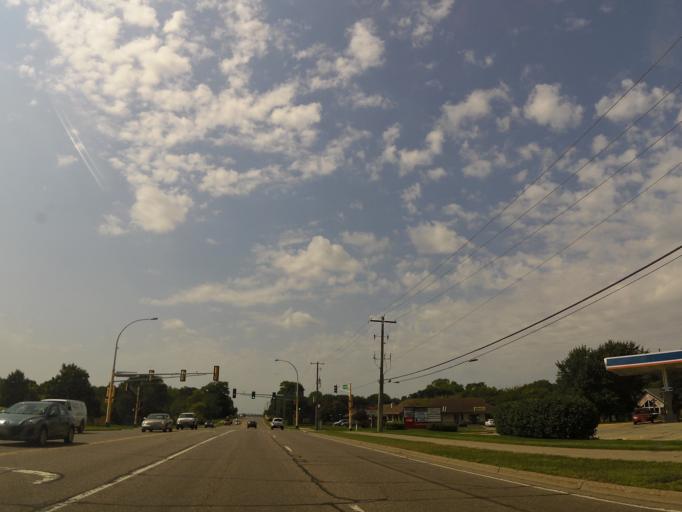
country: US
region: Minnesota
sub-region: Dakota County
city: Eagan
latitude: 44.8336
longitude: -93.1795
